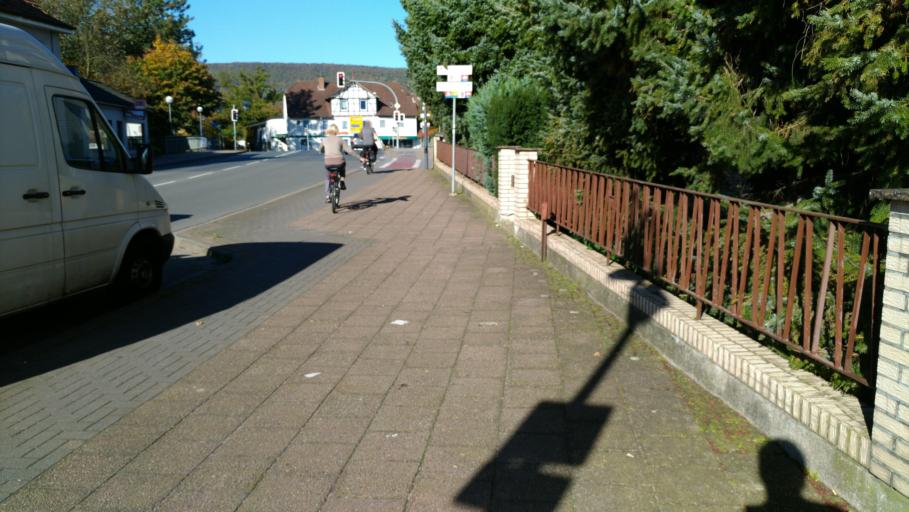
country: DE
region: Lower Saxony
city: Rinteln
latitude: 52.1928
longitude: 9.0821
